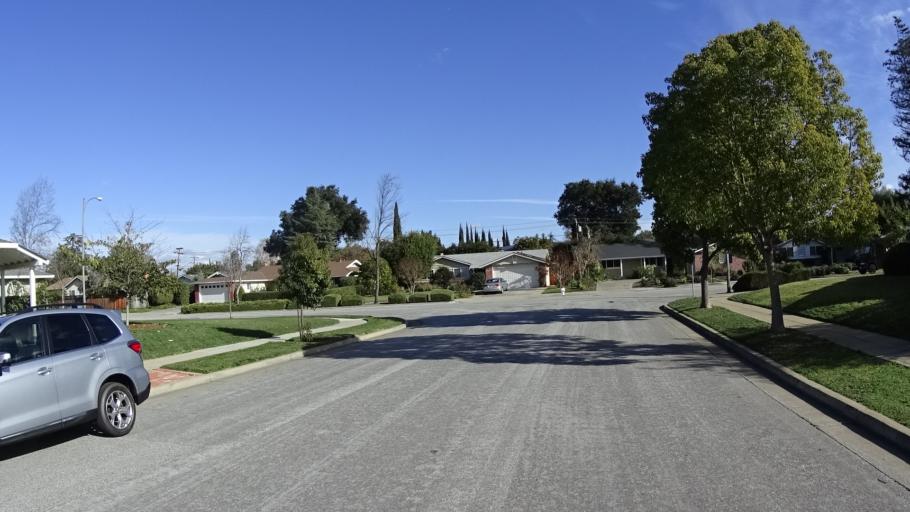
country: US
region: California
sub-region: Santa Clara County
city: Sunnyvale
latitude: 37.3474
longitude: -122.0448
